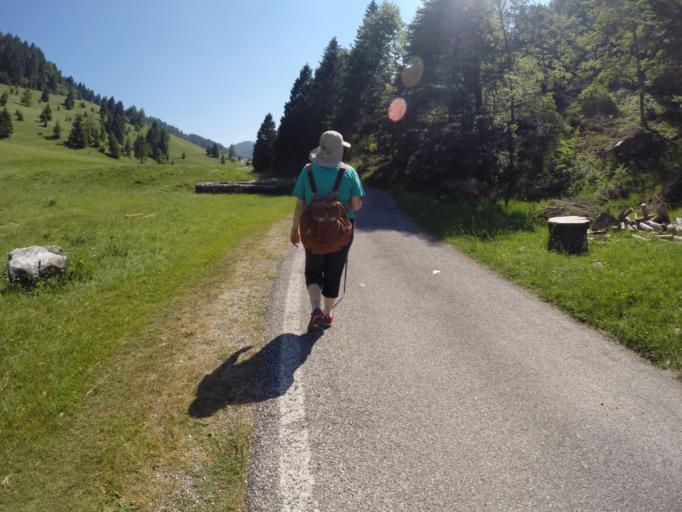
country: IT
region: Veneto
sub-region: Provincia di Treviso
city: Crespano del Grappa
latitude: 45.8900
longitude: 11.8187
